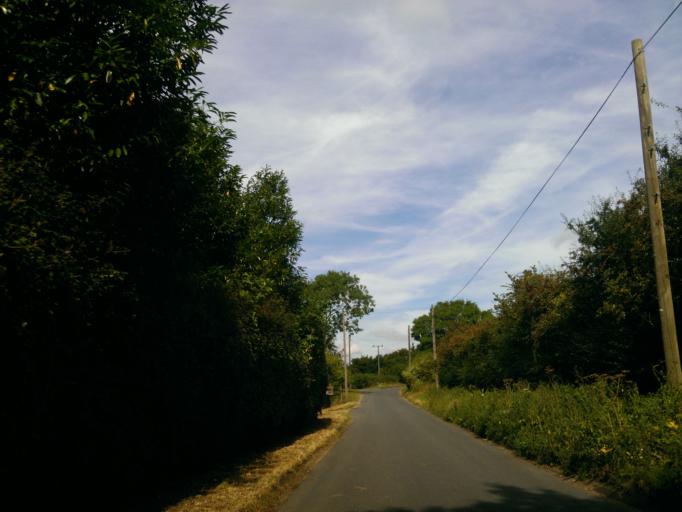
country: GB
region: England
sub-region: Essex
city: Sible Hedingham
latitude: 51.9710
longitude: 0.6216
